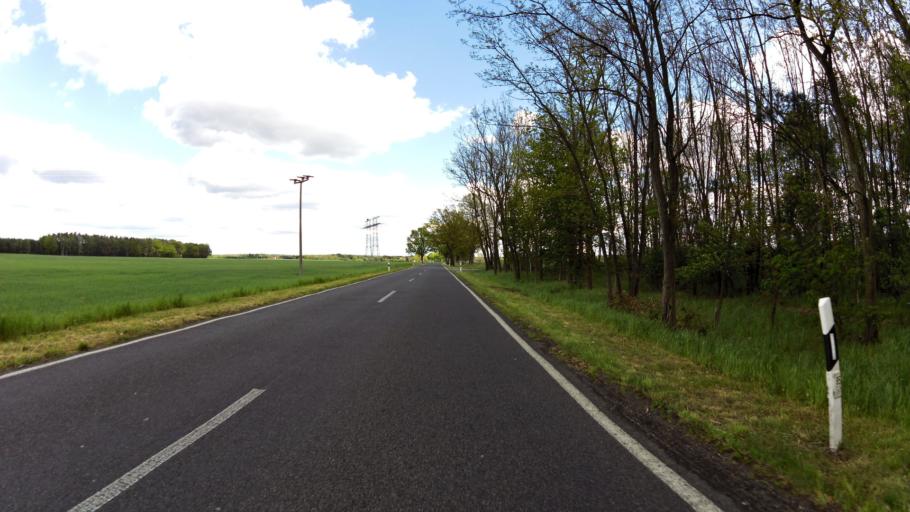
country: DE
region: Brandenburg
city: Wendisch Rietz
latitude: 52.1667
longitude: 14.0577
